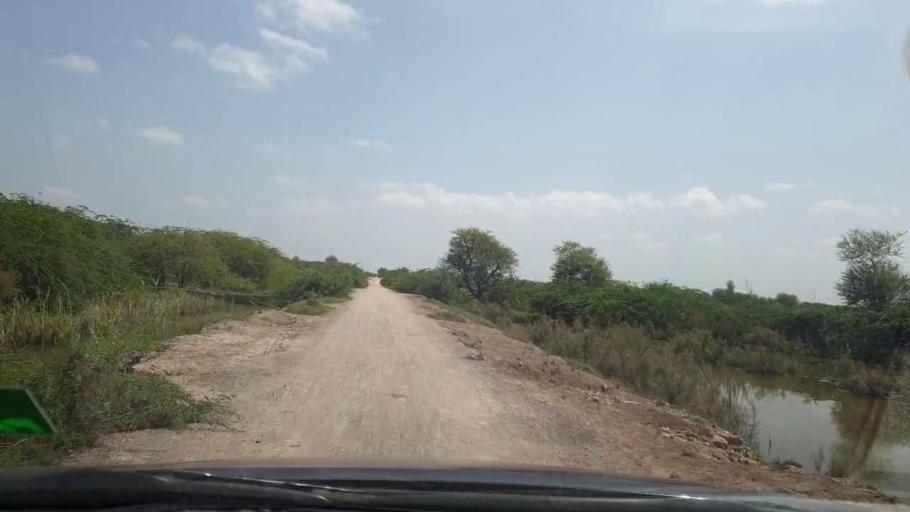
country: PK
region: Sindh
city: Tando Bago
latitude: 24.8603
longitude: 69.1035
